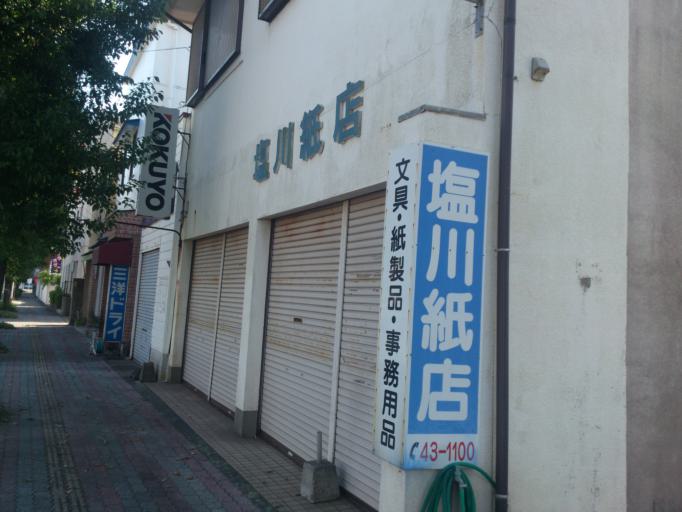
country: JP
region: Kagoshima
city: Kanoya
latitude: 31.3808
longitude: 130.8527
